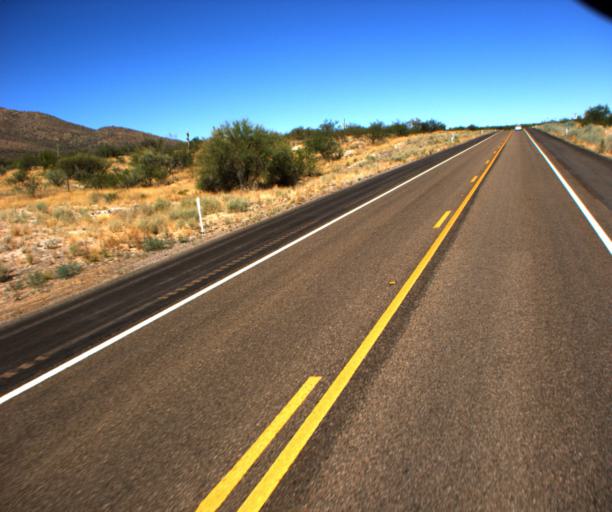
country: US
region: Arizona
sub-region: Pima County
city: Three Points
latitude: 32.0366
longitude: -111.5339
